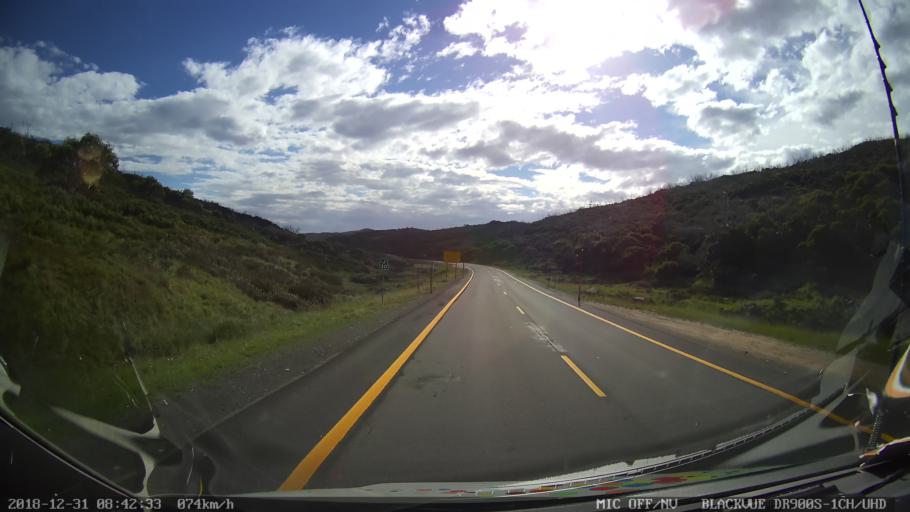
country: AU
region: New South Wales
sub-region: Snowy River
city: Jindabyne
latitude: -36.3930
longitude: 148.4339
